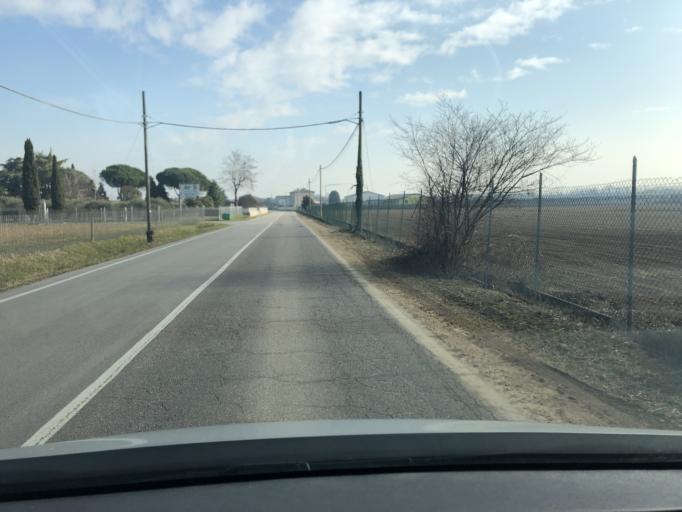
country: IT
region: Veneto
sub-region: Provincia di Verona
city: Sona
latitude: 45.4322
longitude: 10.8506
